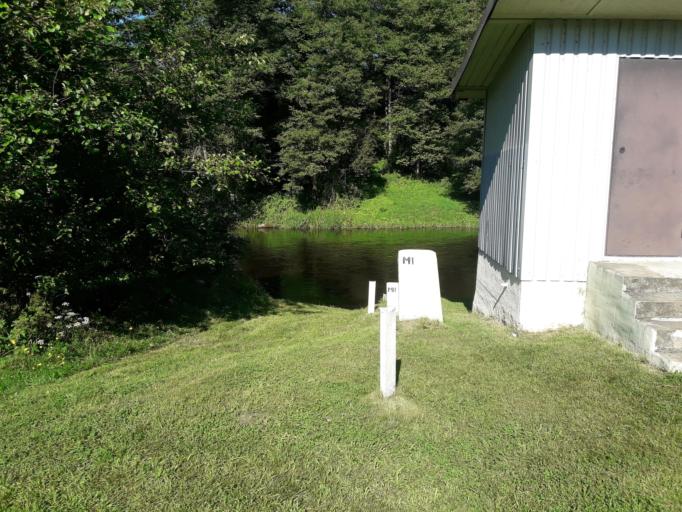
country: LT
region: Alytaus apskritis
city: Druskininkai
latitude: 54.1164
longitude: 24.2133
